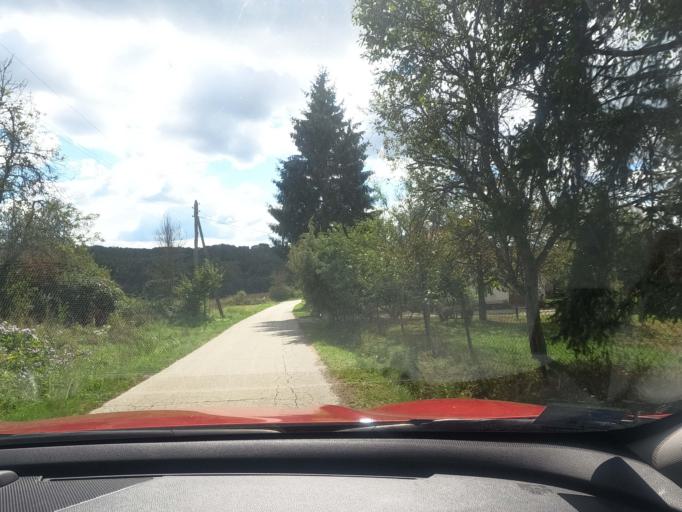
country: HR
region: Karlovacka
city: Vojnic
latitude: 45.2272
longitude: 15.7089
